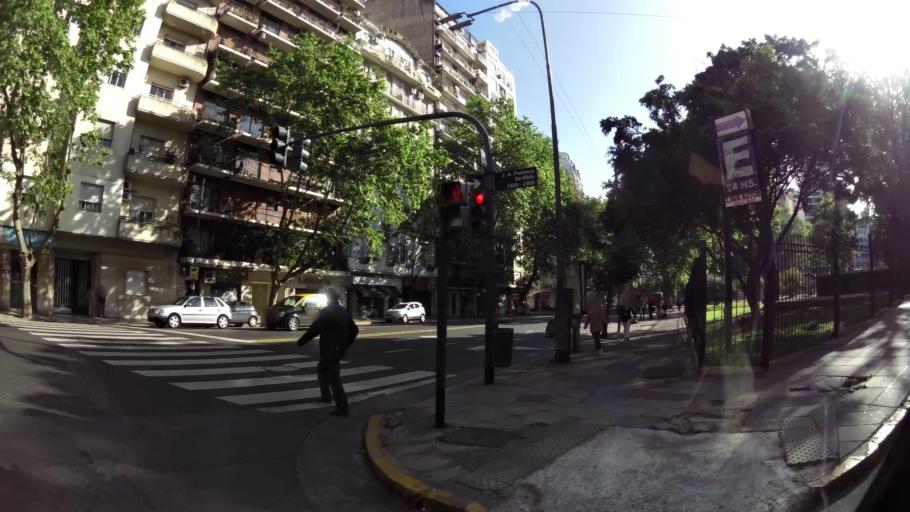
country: AR
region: Buenos Aires F.D.
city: Retiro
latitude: -34.5884
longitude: -58.3986
